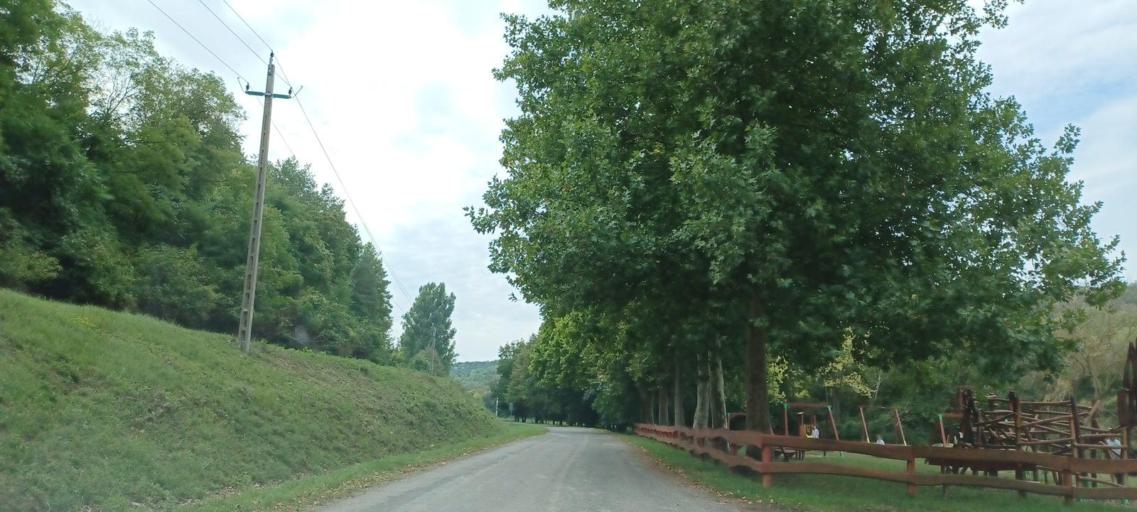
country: HU
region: Tolna
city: Szentgalpuszta
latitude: 46.3561
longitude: 18.6186
